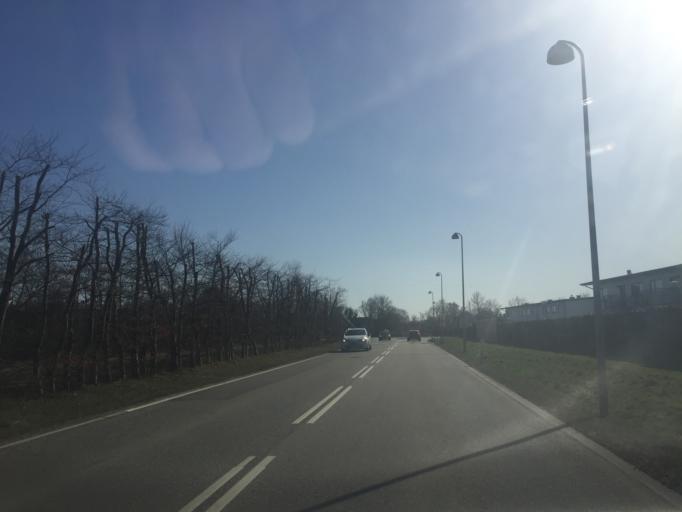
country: DK
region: Capital Region
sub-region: Glostrup Kommune
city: Glostrup
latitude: 55.6826
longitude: 12.4197
